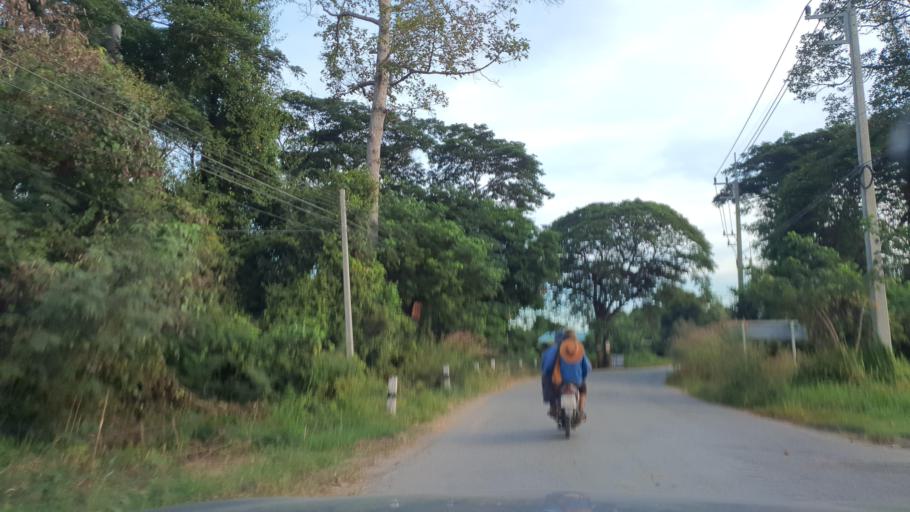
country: TH
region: Nakhon Sawan
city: Nakhon Sawan
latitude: 15.6632
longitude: 100.0596
